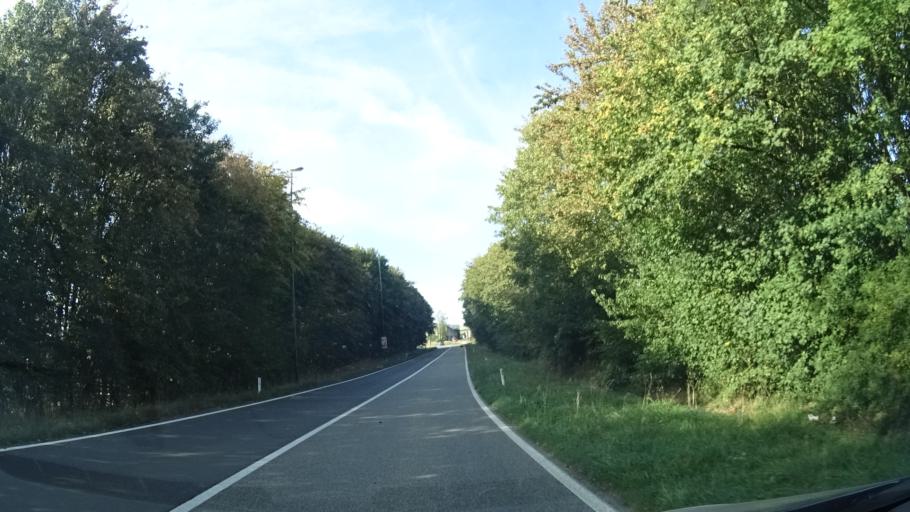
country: BE
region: Wallonia
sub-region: Province de Namur
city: Cerfontaine
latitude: 50.2236
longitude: 4.3812
